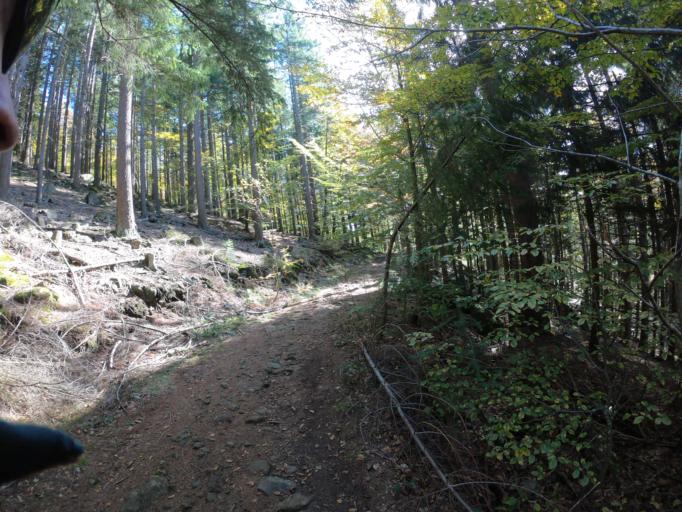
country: DE
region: Bavaria
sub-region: Lower Bavaria
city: Bodenmais
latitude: 49.0839
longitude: 13.1145
